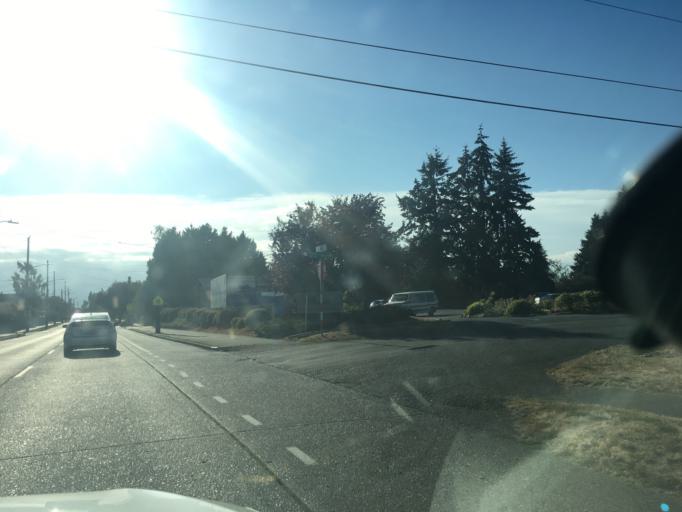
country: US
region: Washington
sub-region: King County
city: Shoreline
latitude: 47.6906
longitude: -122.3886
